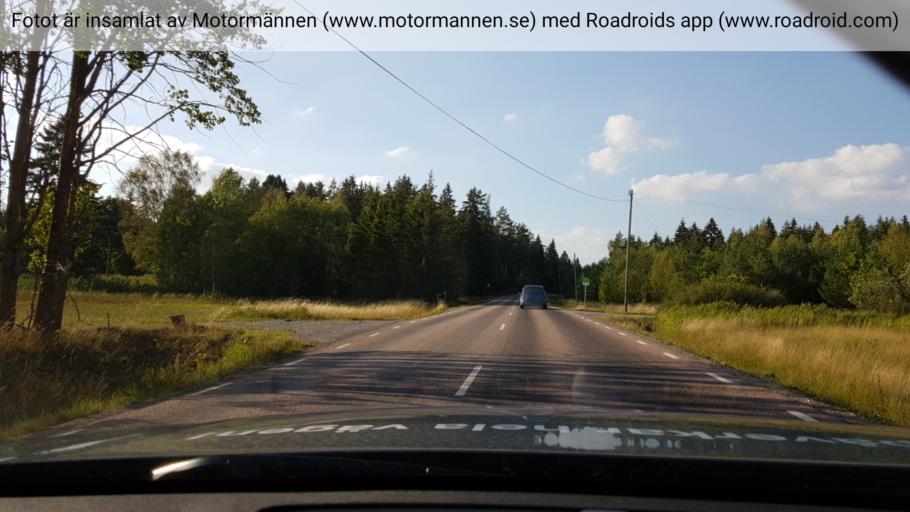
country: SE
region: Soedermanland
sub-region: Strangnas Kommun
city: Mariefred
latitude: 59.2919
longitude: 17.2239
